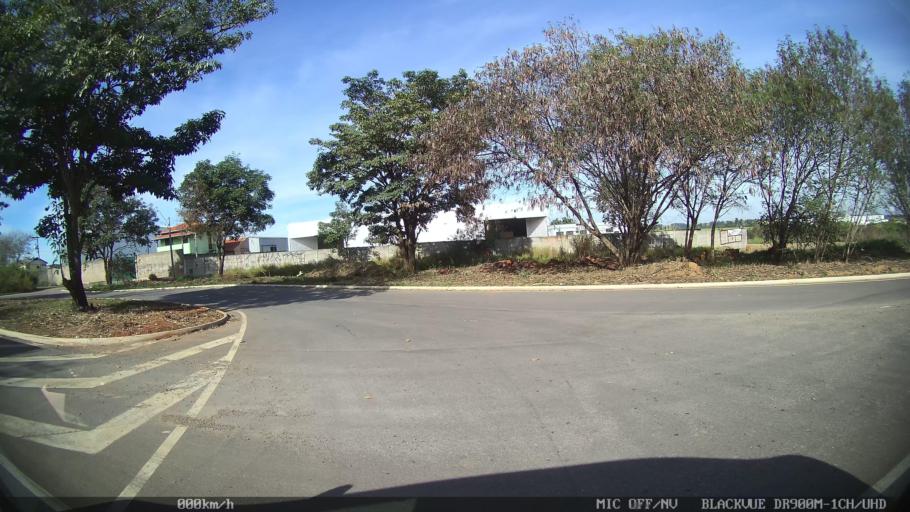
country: BR
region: Sao Paulo
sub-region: Rio Das Pedras
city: Rio das Pedras
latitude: -22.7934
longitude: -47.6203
